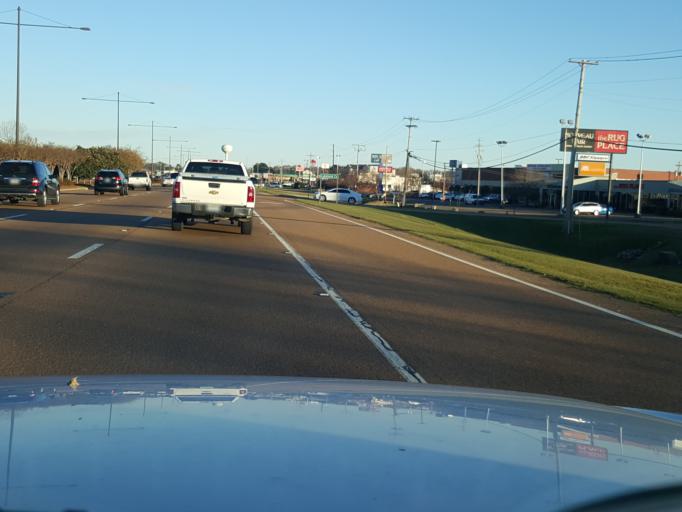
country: US
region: Mississippi
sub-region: Rankin County
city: Flowood
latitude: 32.3302
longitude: -90.1246
